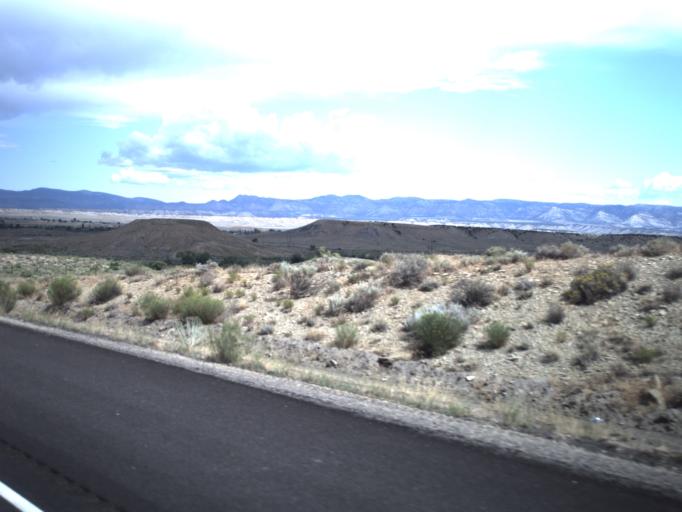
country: US
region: Utah
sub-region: Carbon County
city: Wellington
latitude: 39.5506
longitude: -110.6563
